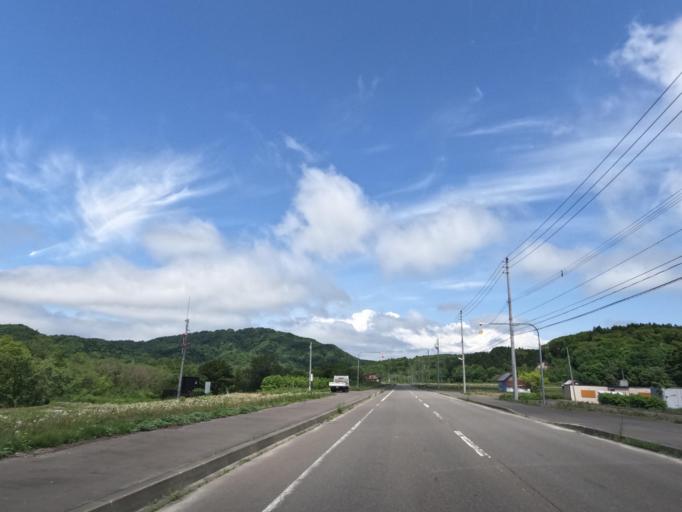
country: JP
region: Hokkaido
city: Tobetsu
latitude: 43.3059
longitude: 141.5537
